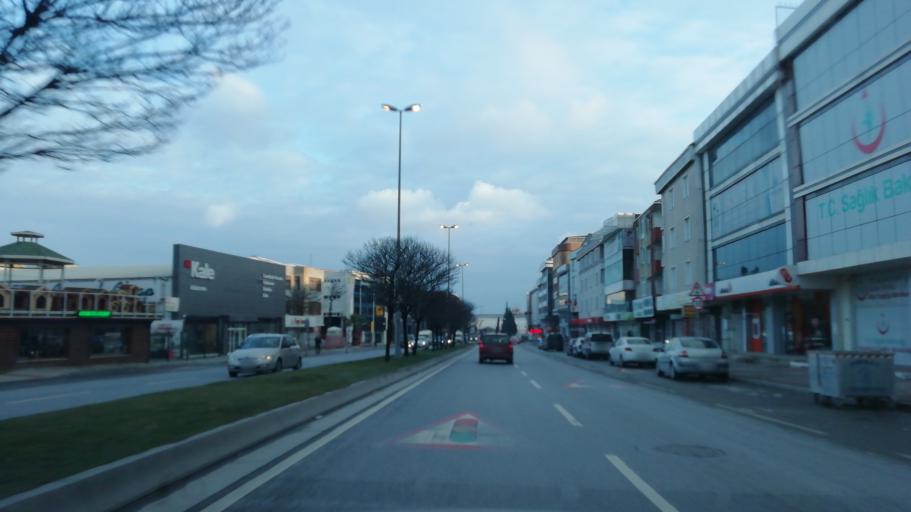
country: TR
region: Istanbul
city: Yakuplu
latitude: 41.0021
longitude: 28.7106
